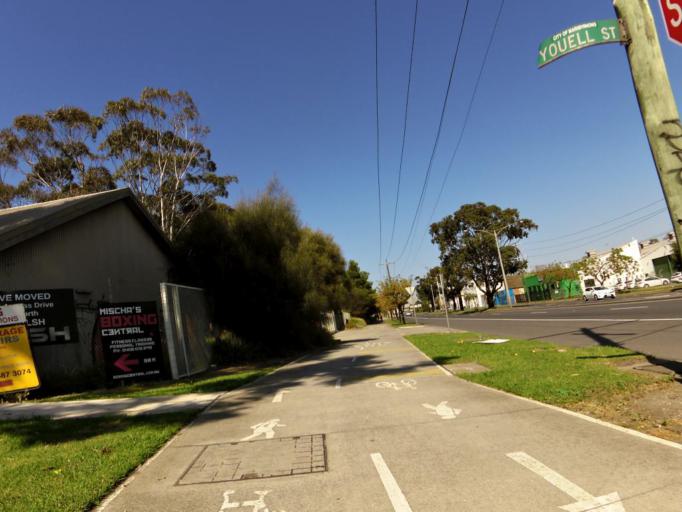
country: AU
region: Victoria
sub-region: Maribyrnong
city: Yarraville
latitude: -37.8099
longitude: 144.9022
